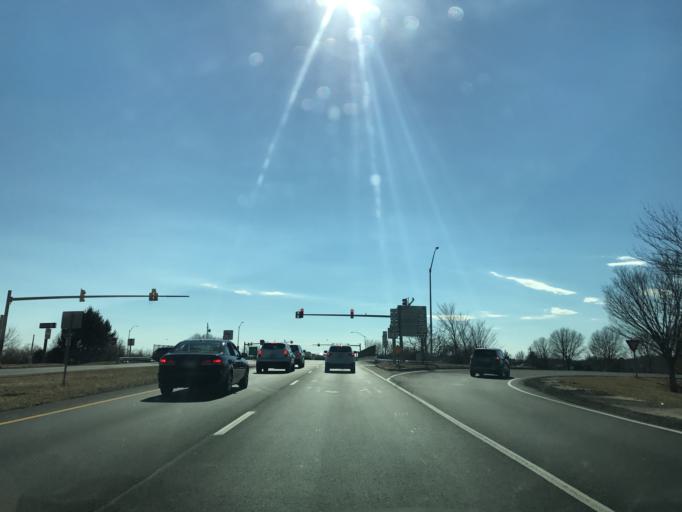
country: US
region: Maryland
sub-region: Queen Anne's County
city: Stevensville
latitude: 38.9801
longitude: -76.3214
